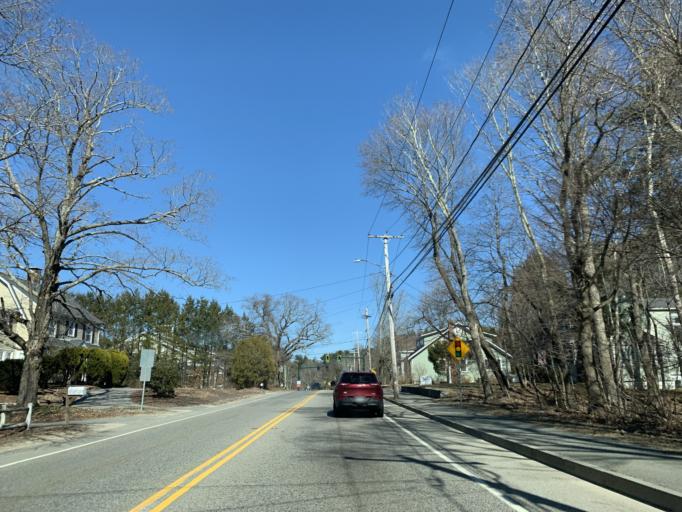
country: US
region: Massachusetts
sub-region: Norfolk County
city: Sharon
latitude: 42.1132
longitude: -71.1878
